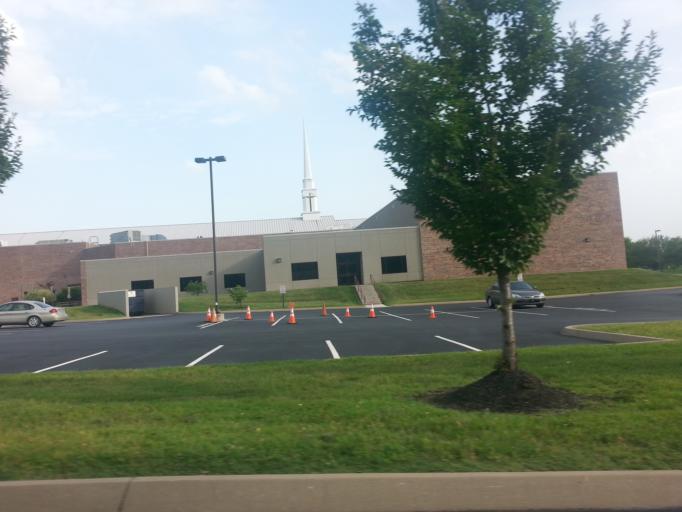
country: US
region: Tennessee
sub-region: Knox County
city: Knoxville
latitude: 35.9041
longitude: -83.9517
